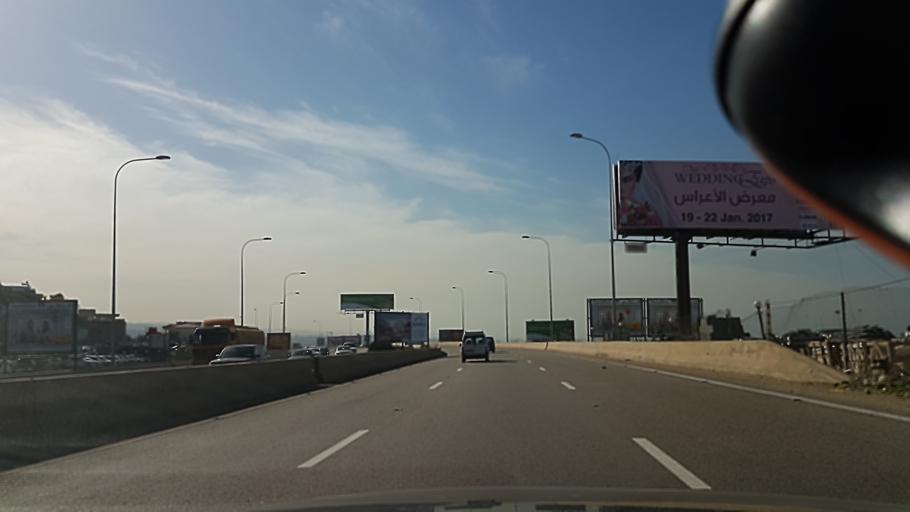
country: LB
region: Liban-Sud
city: Sidon
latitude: 33.6043
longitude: 35.3917
